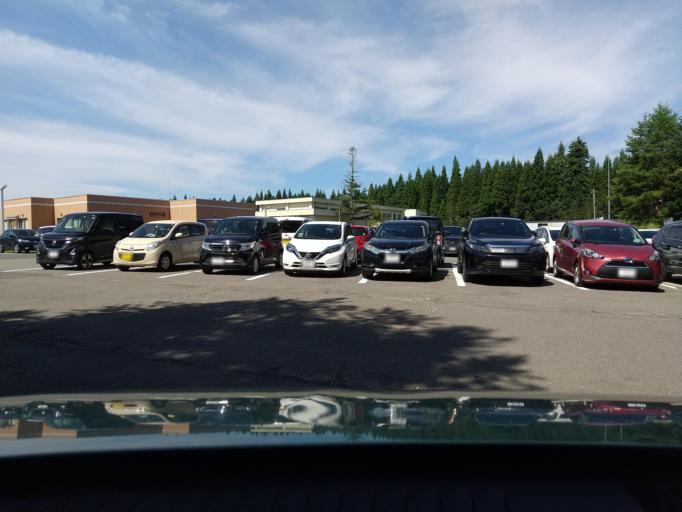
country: JP
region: Akita
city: Akita
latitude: 39.5974
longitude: 140.3038
